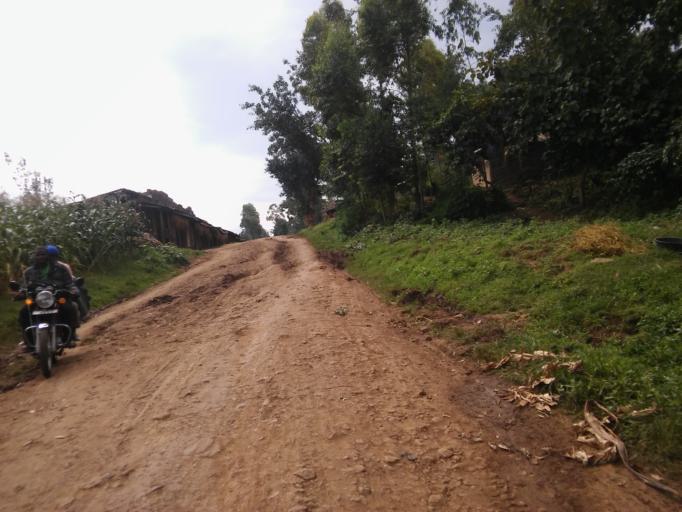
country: UG
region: Eastern Region
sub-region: Manafwa District
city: Manafwa
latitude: 0.8977
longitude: 34.3574
